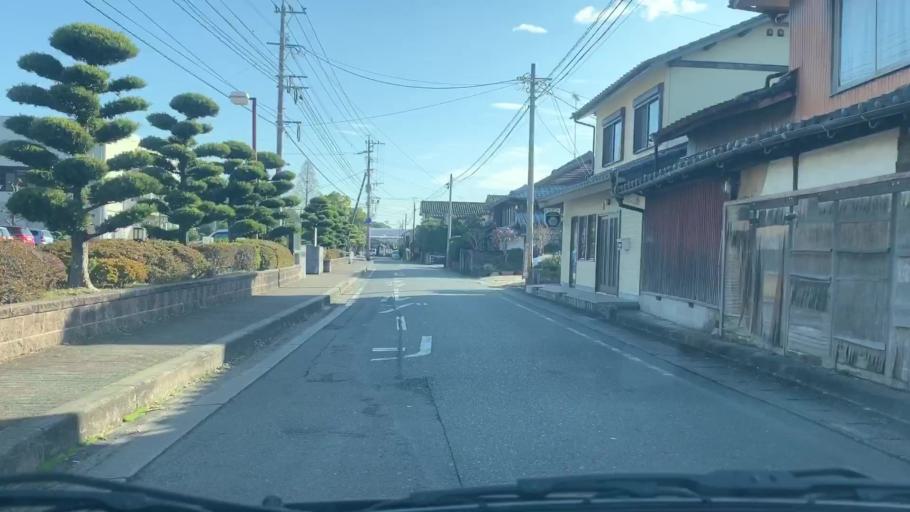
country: JP
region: Saga Prefecture
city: Takeocho-takeo
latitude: 33.2207
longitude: 130.0599
